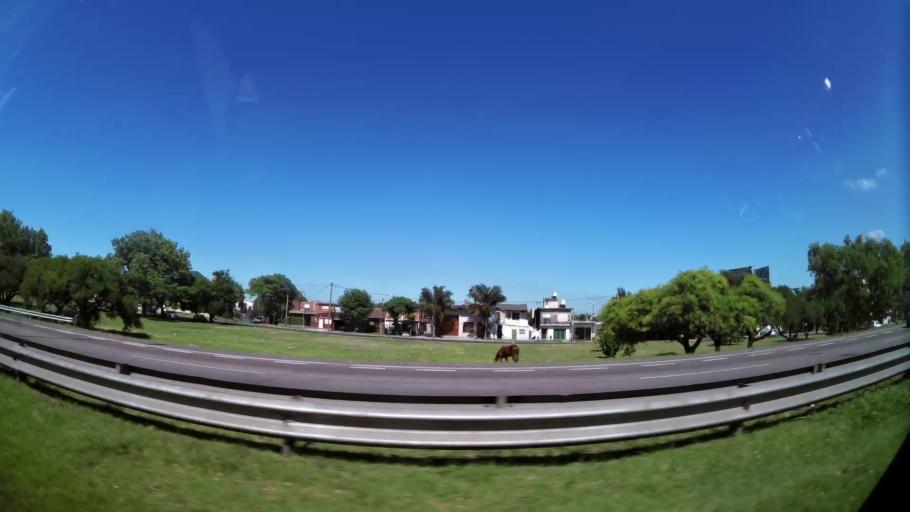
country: AR
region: Buenos Aires
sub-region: Partido de Tigre
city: Tigre
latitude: -34.4624
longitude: -58.5714
